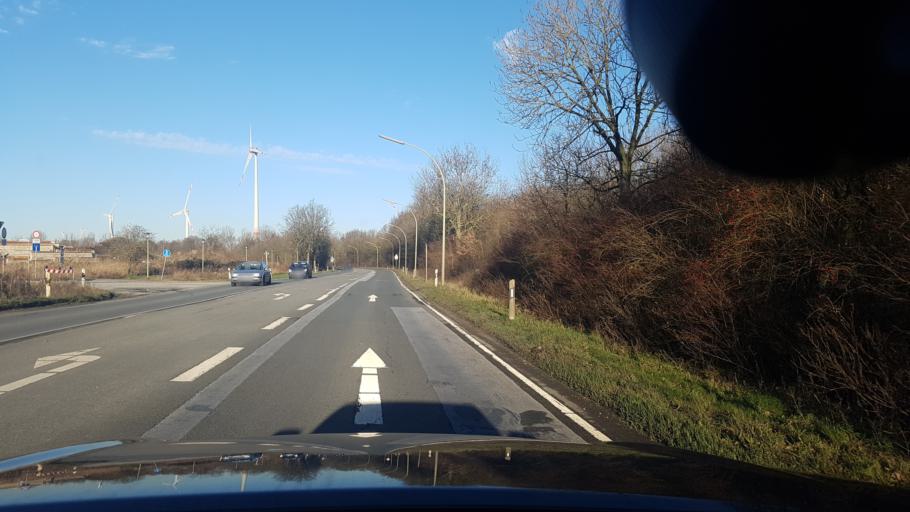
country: DE
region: Lower Saxony
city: Langen
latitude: 53.5845
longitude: 8.5699
